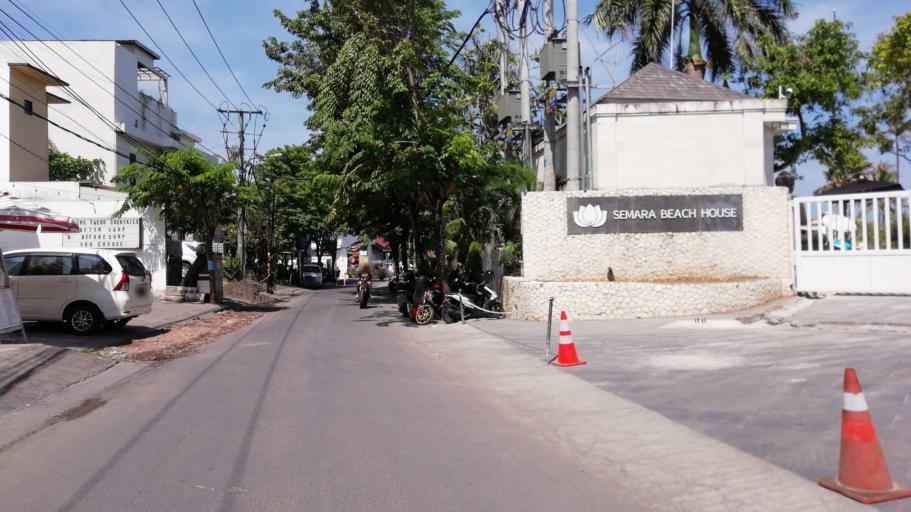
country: ID
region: Bali
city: Banjar Kerobokan
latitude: -8.6661
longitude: 115.1400
